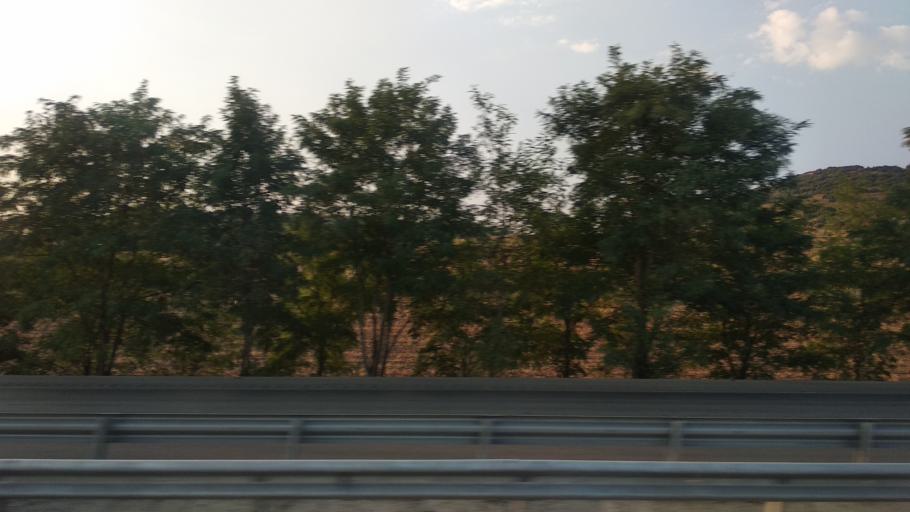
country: TR
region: Manisa
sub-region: Kula
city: Kula
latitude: 38.5607
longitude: 28.7078
